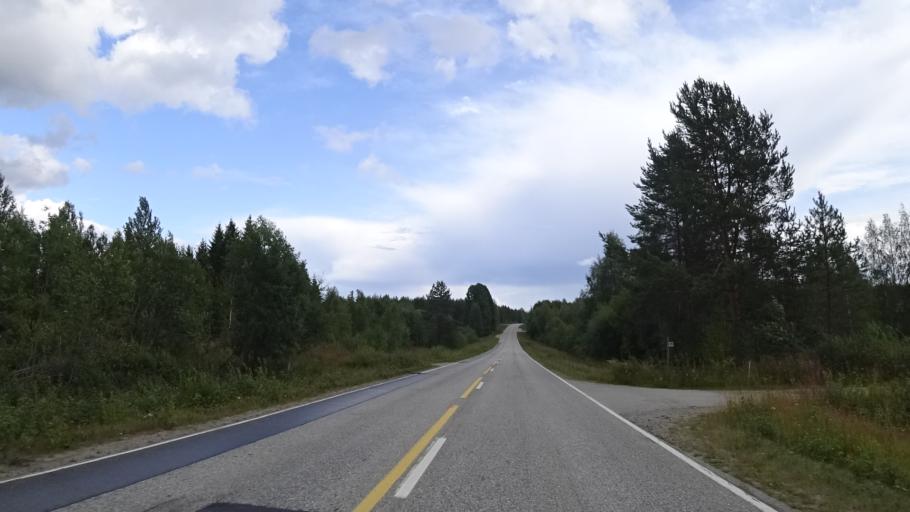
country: FI
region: North Karelia
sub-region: Joensuu
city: Ilomantsi
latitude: 62.6478
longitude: 31.0234
